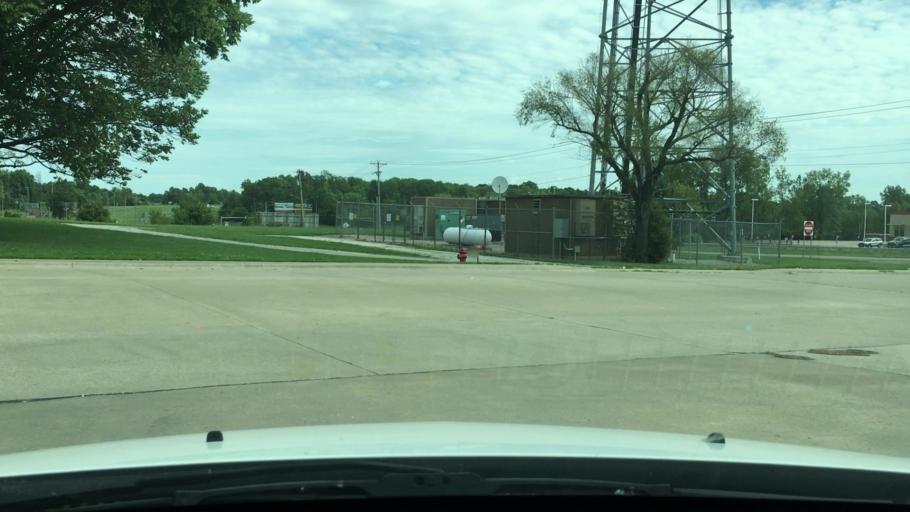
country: US
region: Missouri
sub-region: Callaway County
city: Fulton
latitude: 38.9464
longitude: -91.9420
